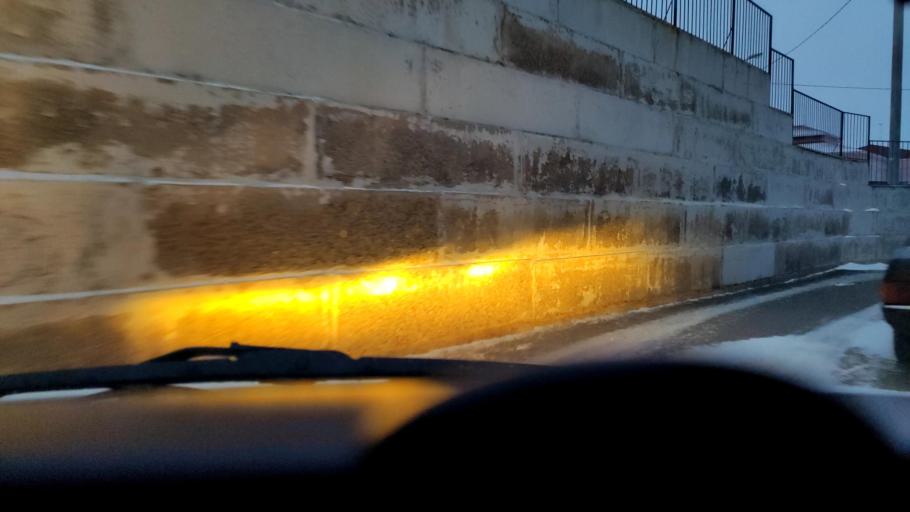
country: RU
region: Voronezj
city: Pridonskoy
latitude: 51.7055
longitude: 39.1073
